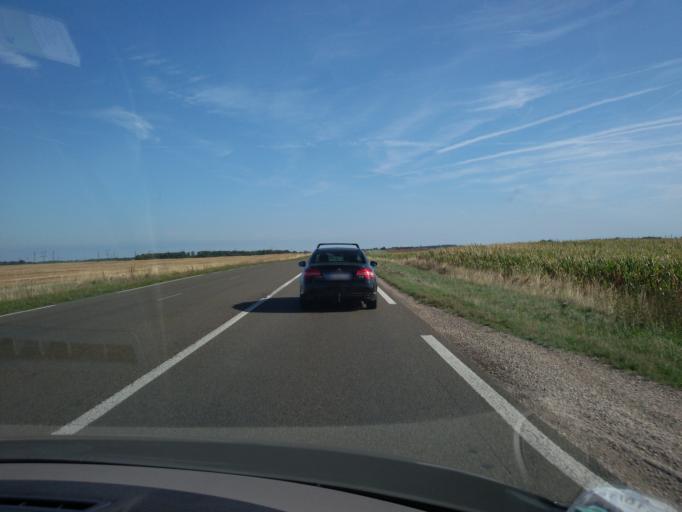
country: FR
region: Ile-de-France
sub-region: Departement de l'Essonne
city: Angerville
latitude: 48.2725
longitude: 1.9751
